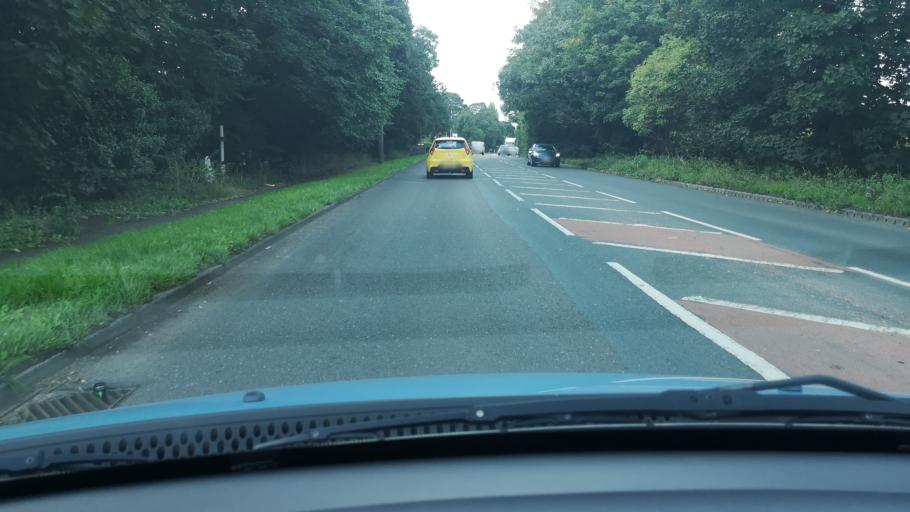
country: GB
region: England
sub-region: Doncaster
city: Kirk Sandall
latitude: 53.5547
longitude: -1.0586
